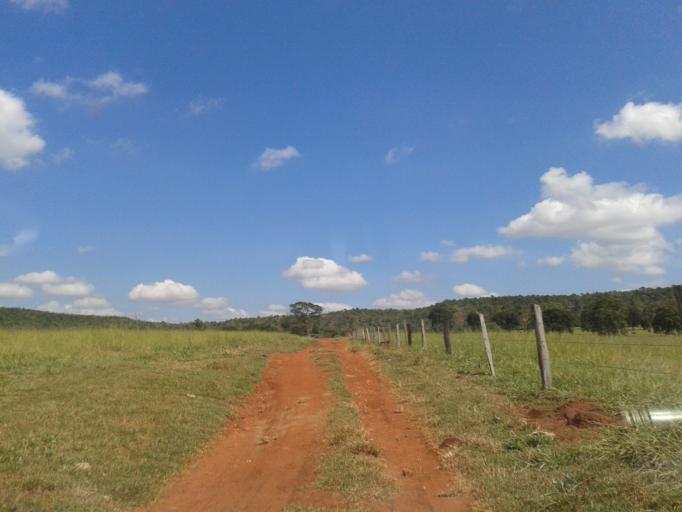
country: BR
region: Minas Gerais
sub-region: Santa Vitoria
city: Santa Vitoria
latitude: -19.2507
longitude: -50.0591
